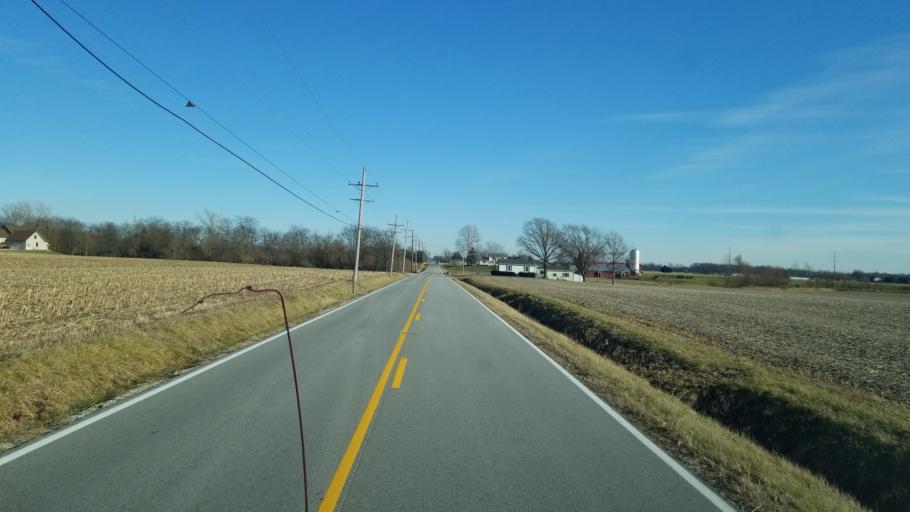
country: US
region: Ohio
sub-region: Sandusky County
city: Stony Prairie
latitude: 41.3493
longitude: -83.1834
